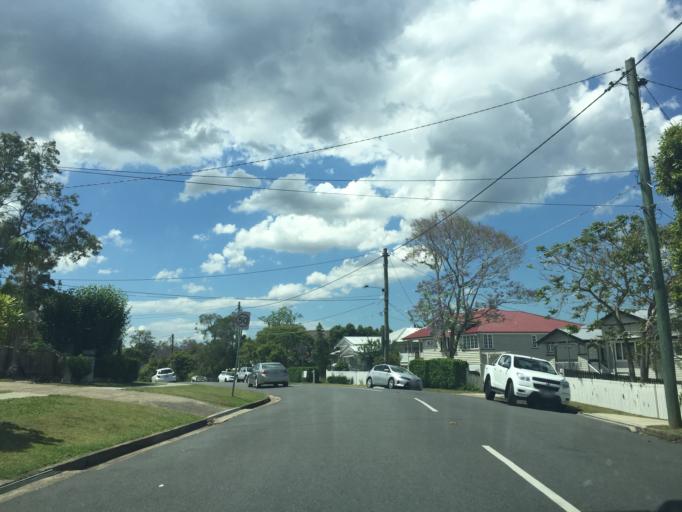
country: AU
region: Queensland
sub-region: Brisbane
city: Milton
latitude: -27.4465
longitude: 152.9774
